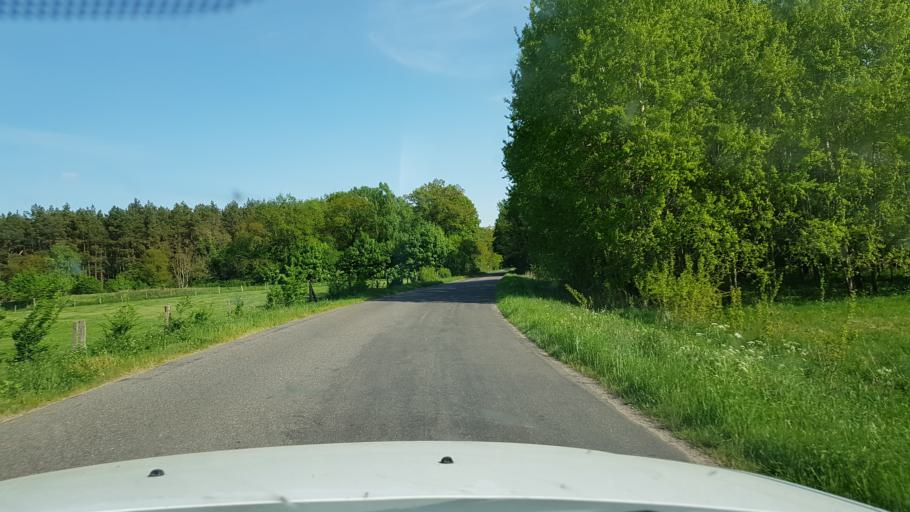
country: PL
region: West Pomeranian Voivodeship
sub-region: Powiat lobeski
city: Resko
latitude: 53.8448
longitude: 15.3674
